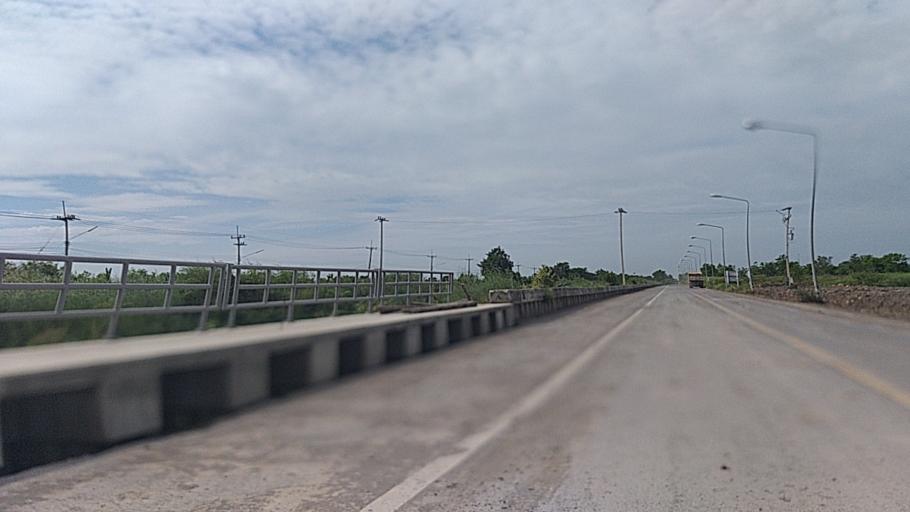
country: TH
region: Pathum Thani
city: Nong Suea
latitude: 14.0688
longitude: 100.8922
